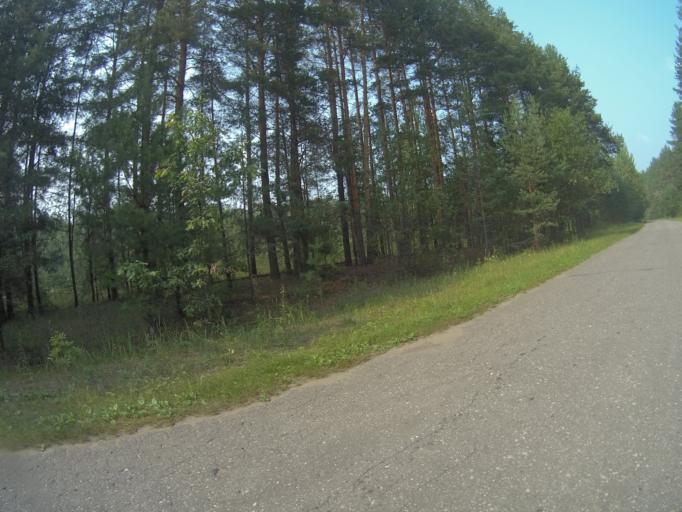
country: RU
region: Vladimir
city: Vorsha
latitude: 56.0199
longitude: 40.1540
